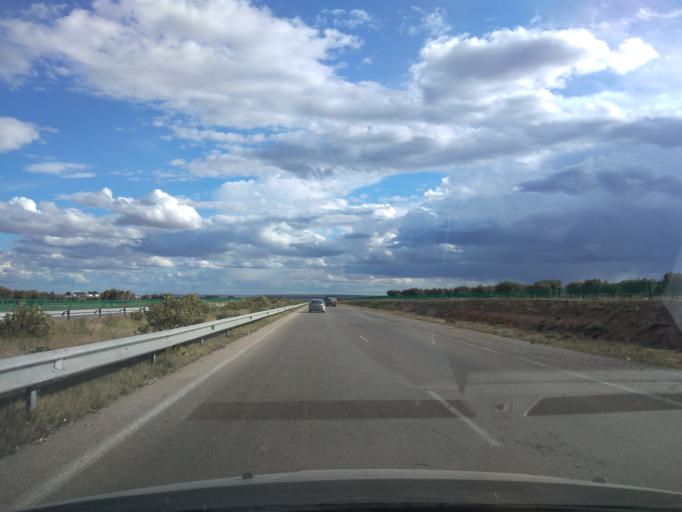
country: TN
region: Al Munastir
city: Manzil Kamil
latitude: 35.5450
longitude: 10.6213
